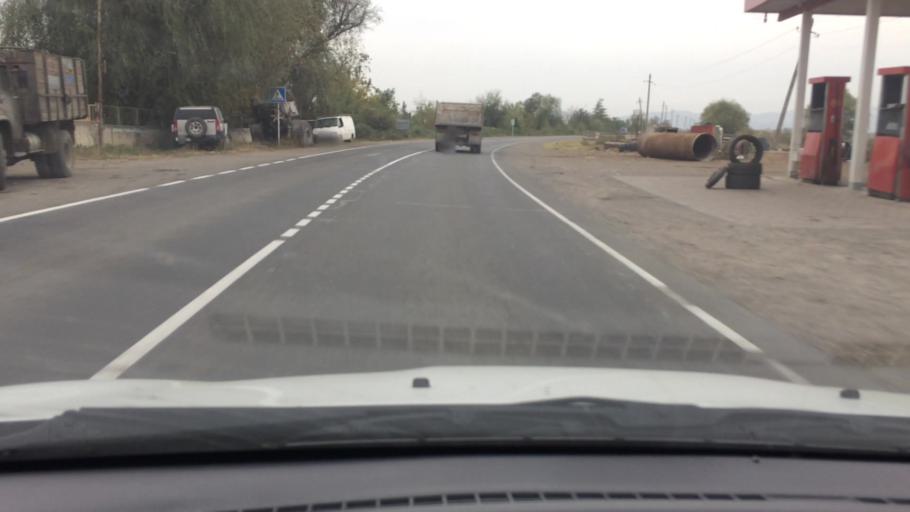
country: GE
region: Kvemo Kartli
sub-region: Marneuli
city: Marneuli
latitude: 41.4721
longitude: 44.8047
